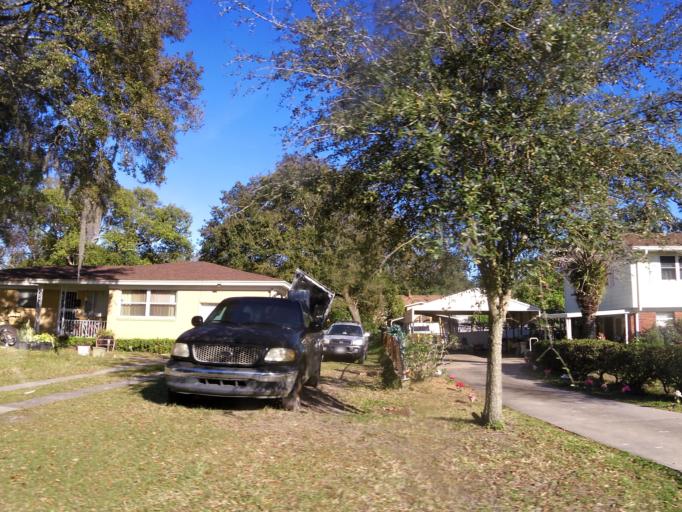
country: US
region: Florida
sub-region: Duval County
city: Jacksonville
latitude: 30.3996
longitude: -81.6769
